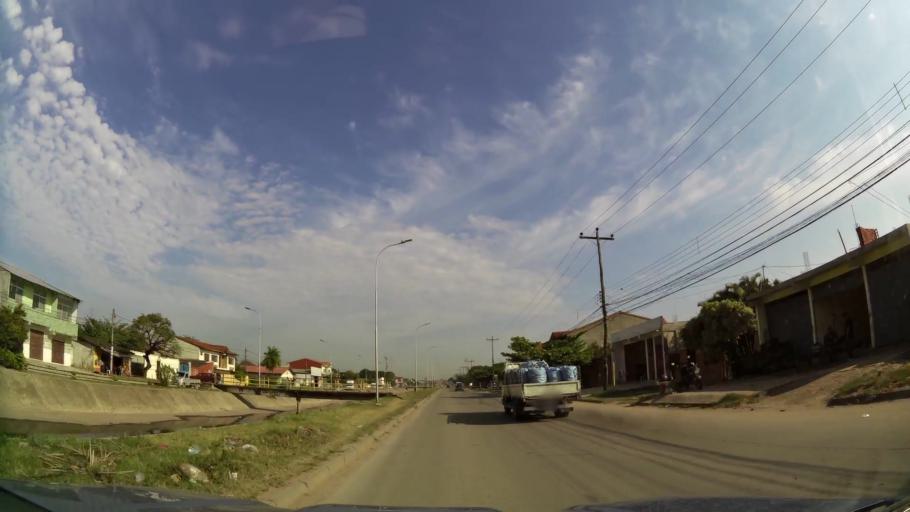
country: BO
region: Santa Cruz
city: Santa Cruz de la Sierra
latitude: -17.7408
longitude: -63.1483
